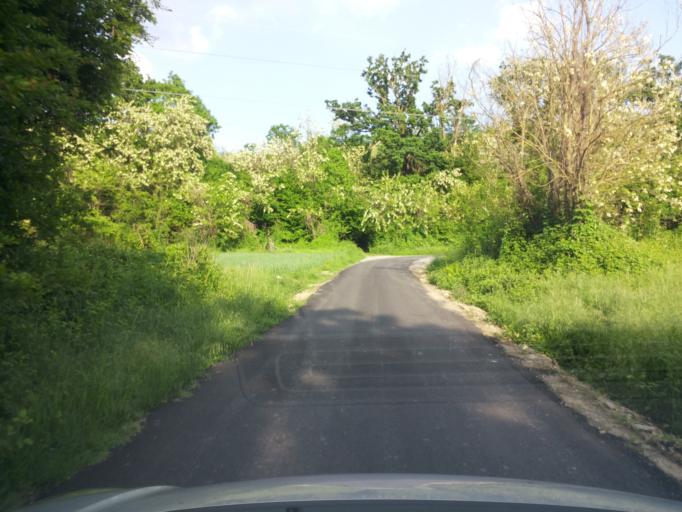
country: IT
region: Piedmont
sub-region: Provincia di Torino
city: Settimo Rottaro
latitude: 45.3996
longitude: 8.0032
